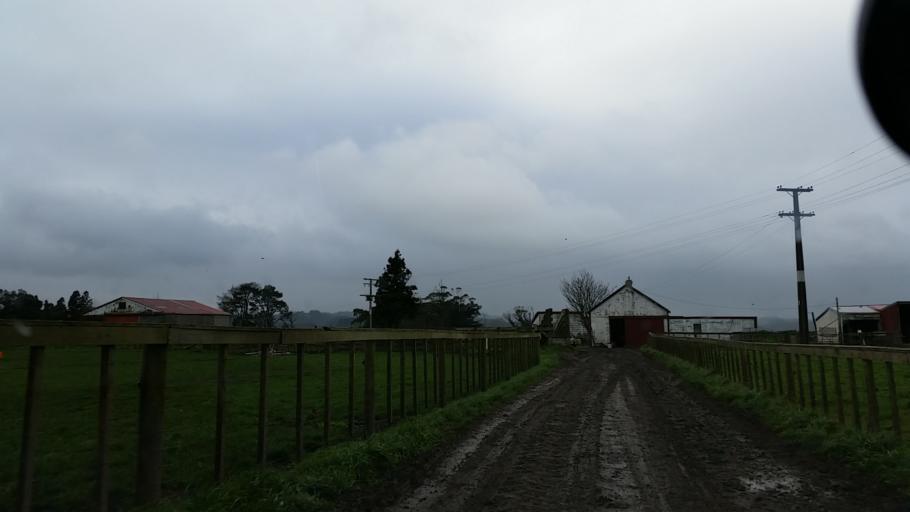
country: NZ
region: Taranaki
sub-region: South Taranaki District
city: Patea
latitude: -39.7696
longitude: 174.7096
